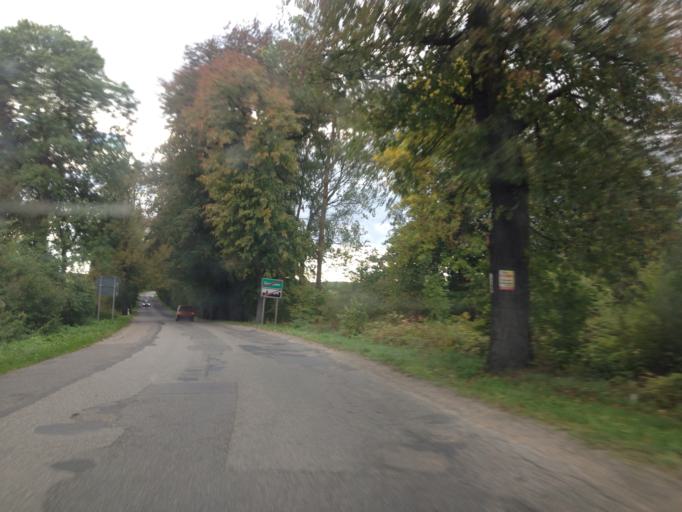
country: PL
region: Pomeranian Voivodeship
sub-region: Powiat kwidzynski
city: Prabuty
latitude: 53.7491
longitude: 19.1788
